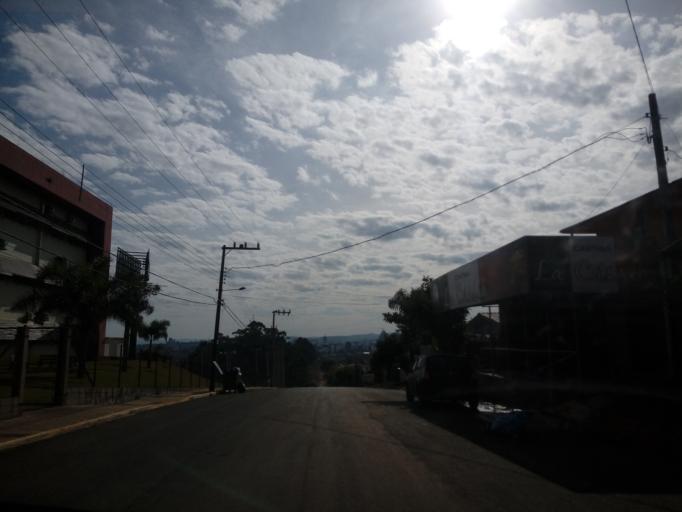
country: BR
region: Santa Catarina
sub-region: Chapeco
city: Chapeco
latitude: -27.1193
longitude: -52.6302
